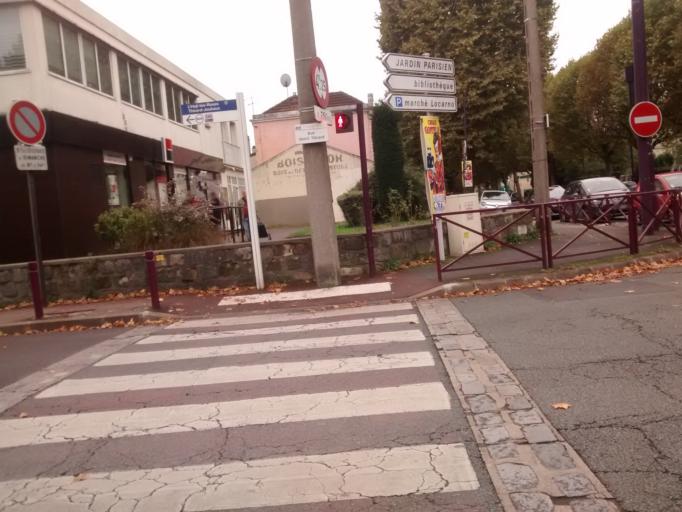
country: FR
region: Ile-de-France
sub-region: Departement du Val-de-Marne
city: L'Hay-les-Roses
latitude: 48.7784
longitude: 2.3409
